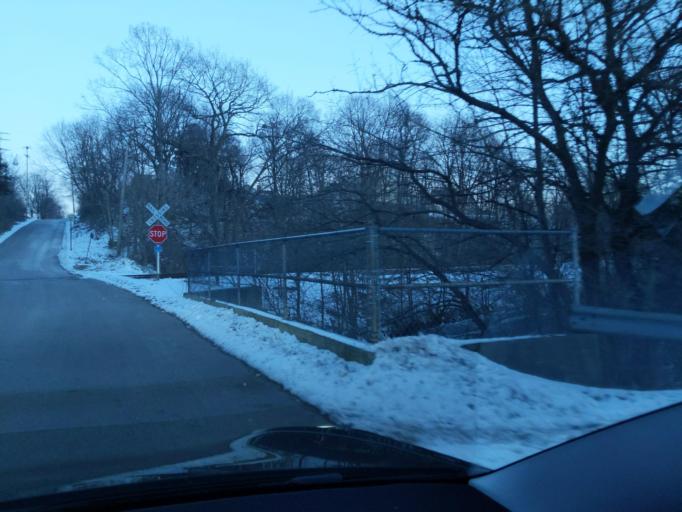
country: US
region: Michigan
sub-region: Ingham County
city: Mason
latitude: 42.5772
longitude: -84.4450
